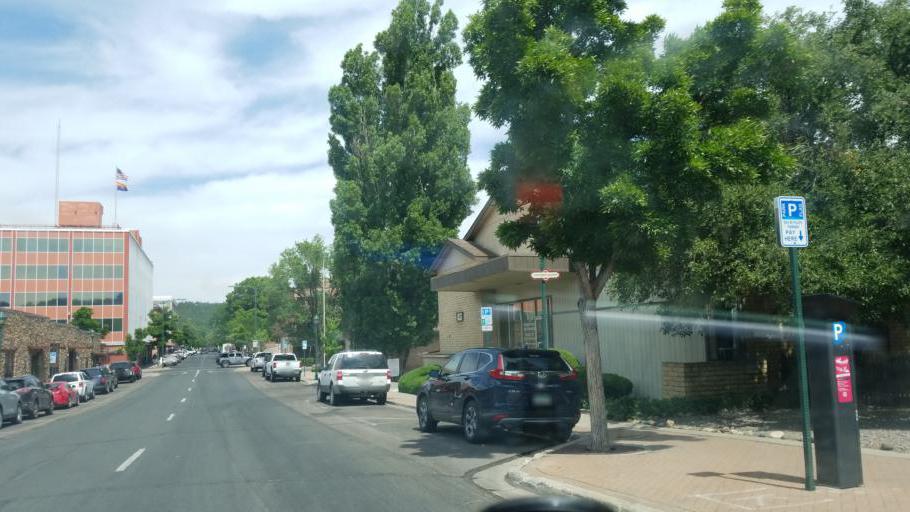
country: US
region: Arizona
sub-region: Coconino County
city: Flagstaff
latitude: 35.1984
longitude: -111.6451
